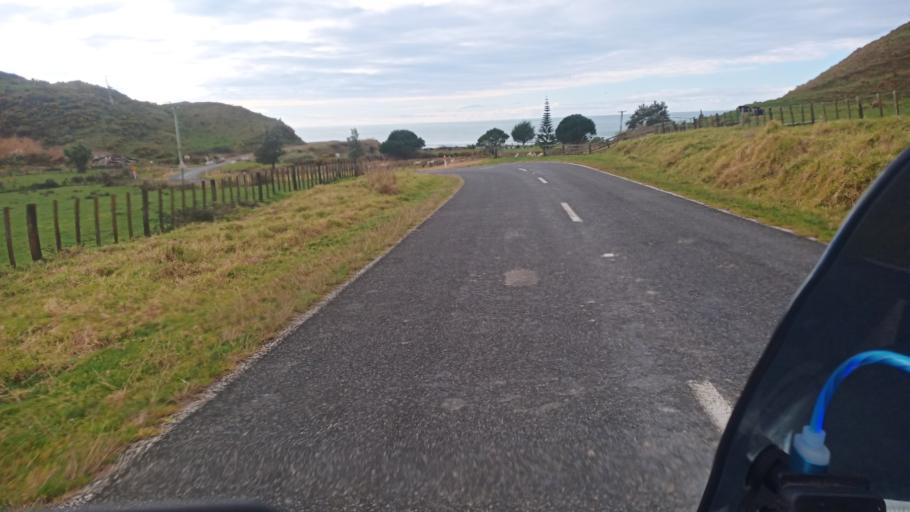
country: NZ
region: Gisborne
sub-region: Gisborne District
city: Gisborne
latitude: -38.3154
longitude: 178.3199
